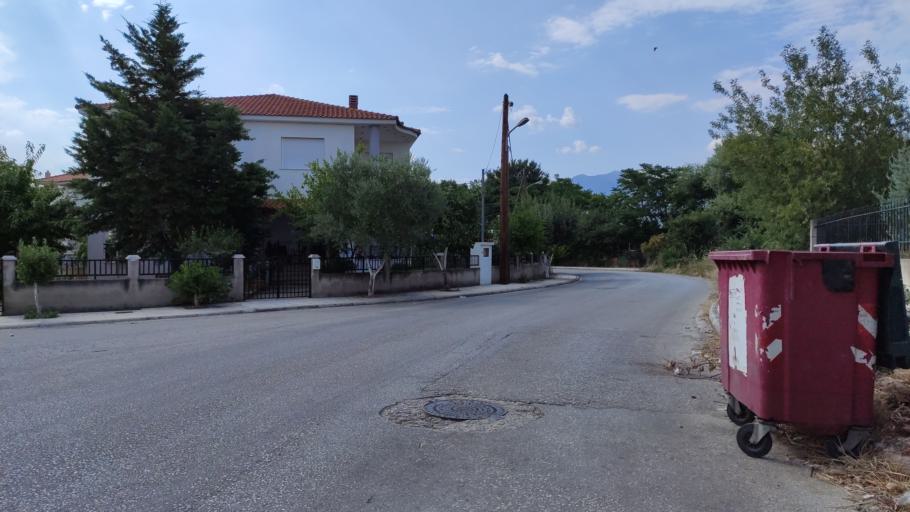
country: GR
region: East Macedonia and Thrace
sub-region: Nomos Rodopis
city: Komotini
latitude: 41.1317
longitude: 25.4000
